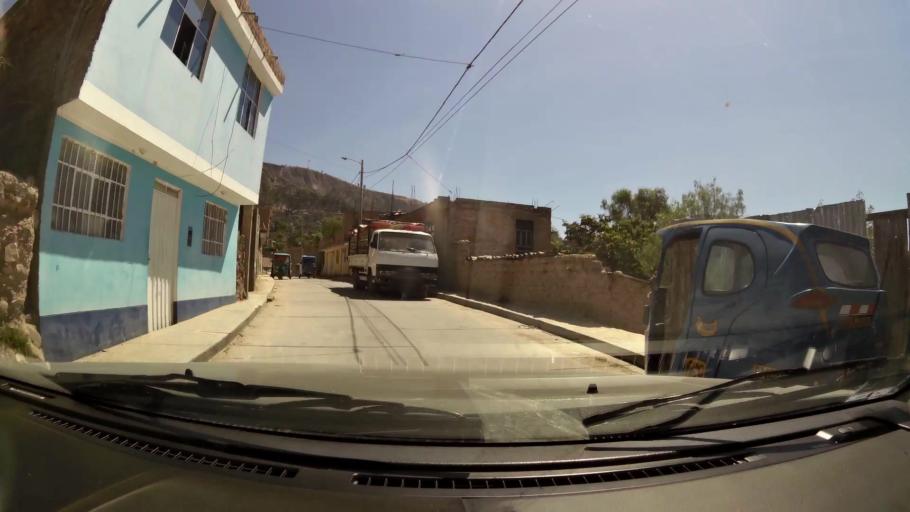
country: PE
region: Ayacucho
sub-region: Provincia de Huamanga
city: Ayacucho
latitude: -13.1662
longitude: -74.2353
